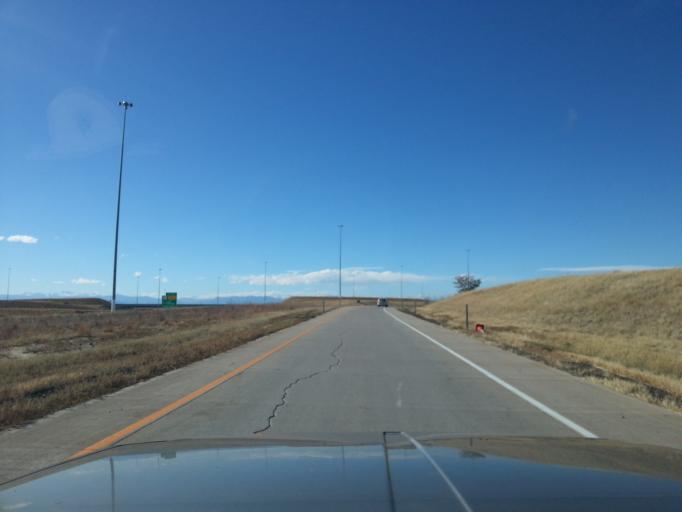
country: US
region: Colorado
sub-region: Adams County
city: Aurora
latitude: 39.8350
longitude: -104.7399
